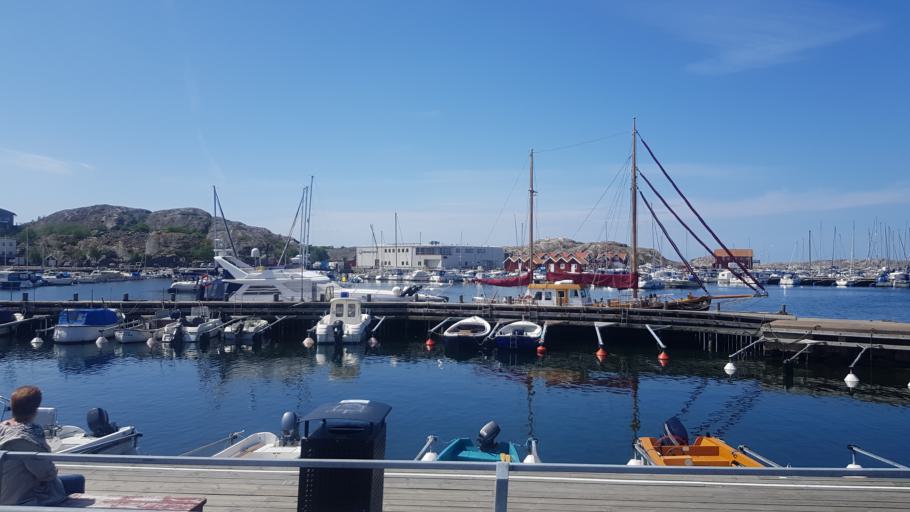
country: SE
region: Vaestra Goetaland
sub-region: Tjorns Kommun
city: Skaerhamn
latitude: 57.9898
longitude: 11.5461
